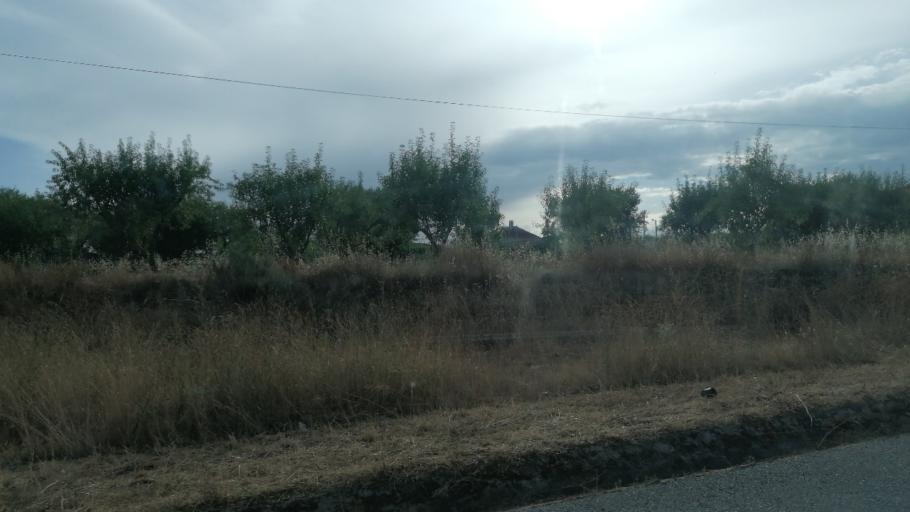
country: PT
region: Viseu
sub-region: Sao Joao da Pesqueira
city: Sao Joao da Pesqueira
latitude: 41.1018
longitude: -7.3820
